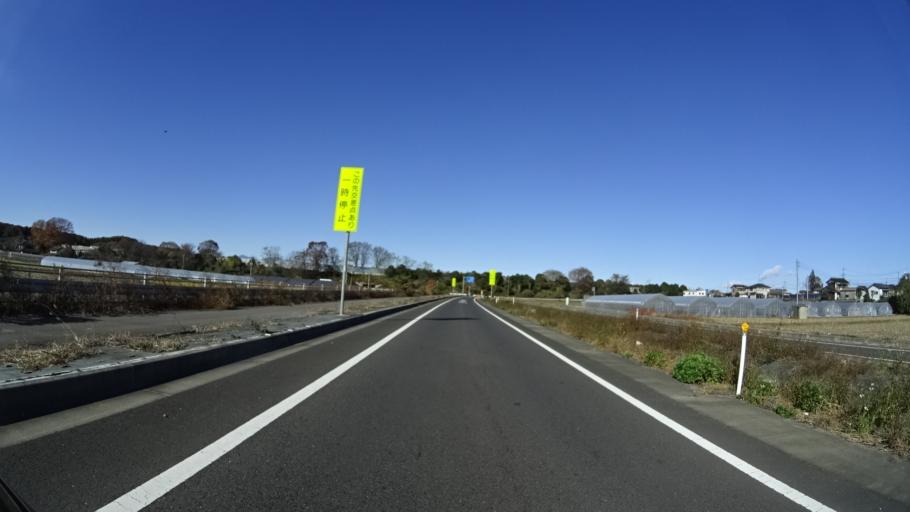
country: JP
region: Tochigi
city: Kanuma
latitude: 36.4942
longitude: 139.7521
